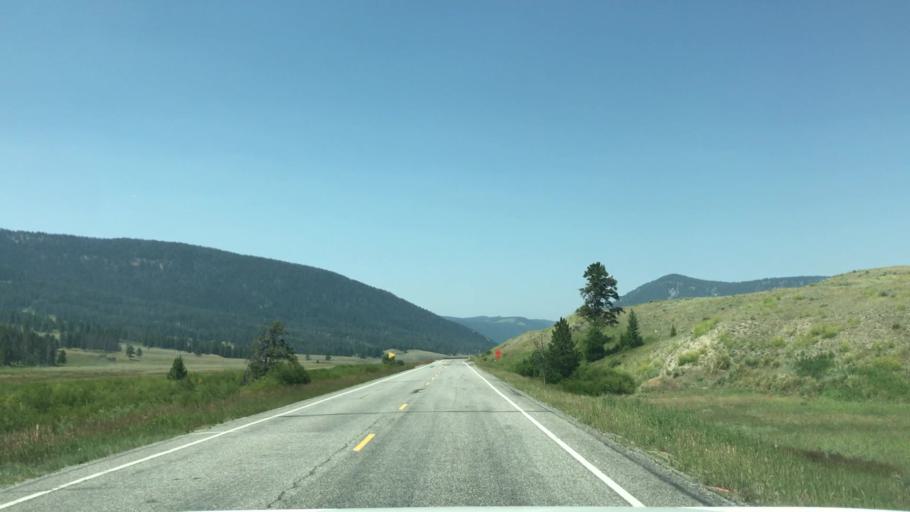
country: US
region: Montana
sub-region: Gallatin County
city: Big Sky
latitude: 45.0412
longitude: -111.1250
